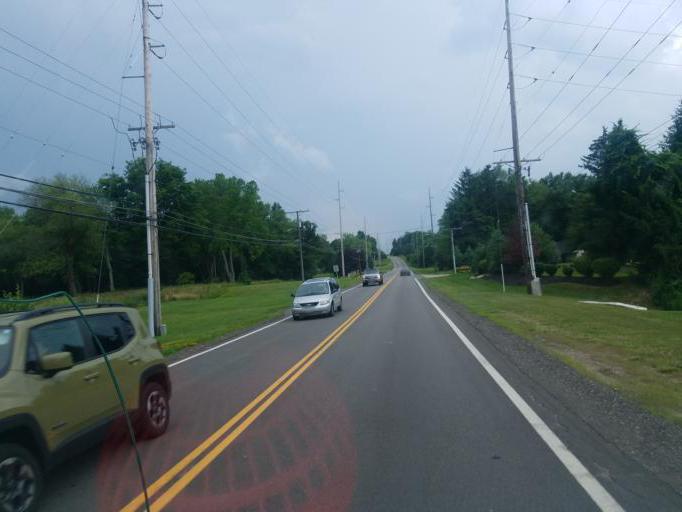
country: US
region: Ohio
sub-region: Medina County
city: Wadsworth
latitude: 41.0403
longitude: -81.7129
